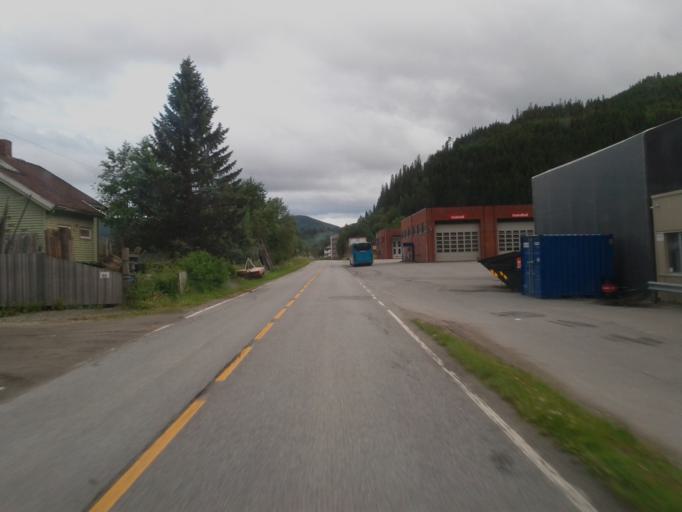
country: NO
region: Sor-Trondelag
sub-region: Midtre Gauldal
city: Storen
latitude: 63.0550
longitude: 10.2853
